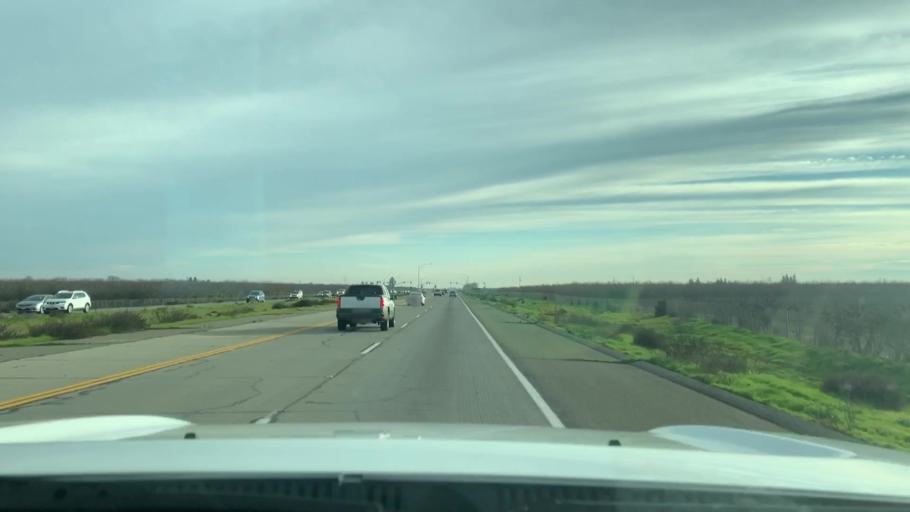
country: US
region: California
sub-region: Fresno County
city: Caruthers
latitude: 36.5232
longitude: -119.7864
